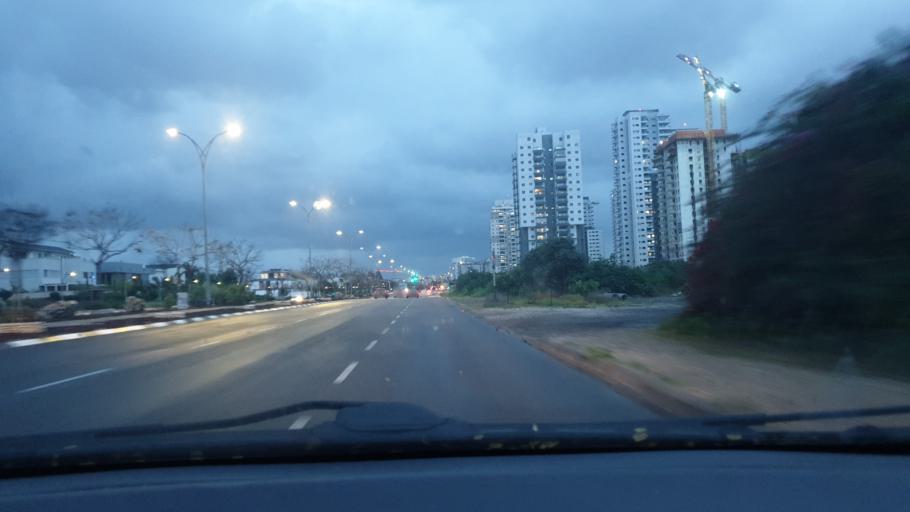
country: IL
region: Central District
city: Rishon LeZiyyon
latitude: 31.9817
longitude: 34.7995
